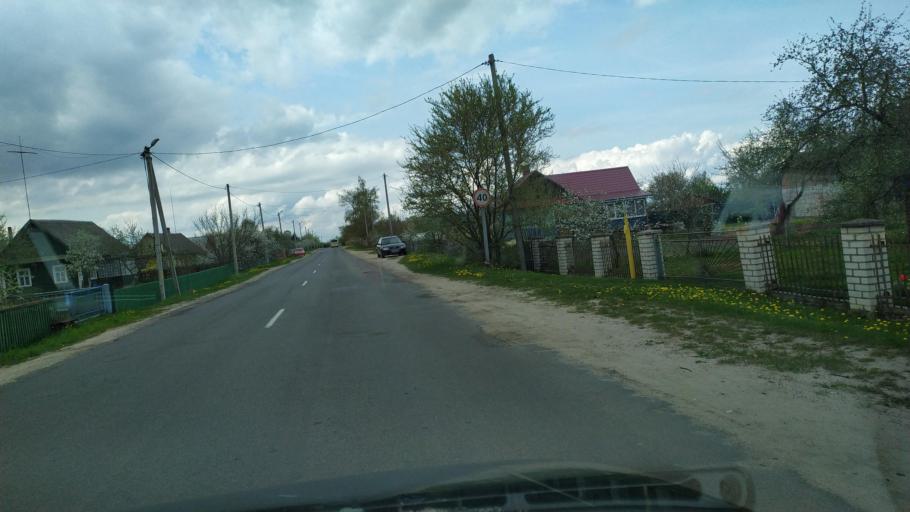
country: BY
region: Brest
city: Pruzhany
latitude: 52.5702
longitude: 24.4168
